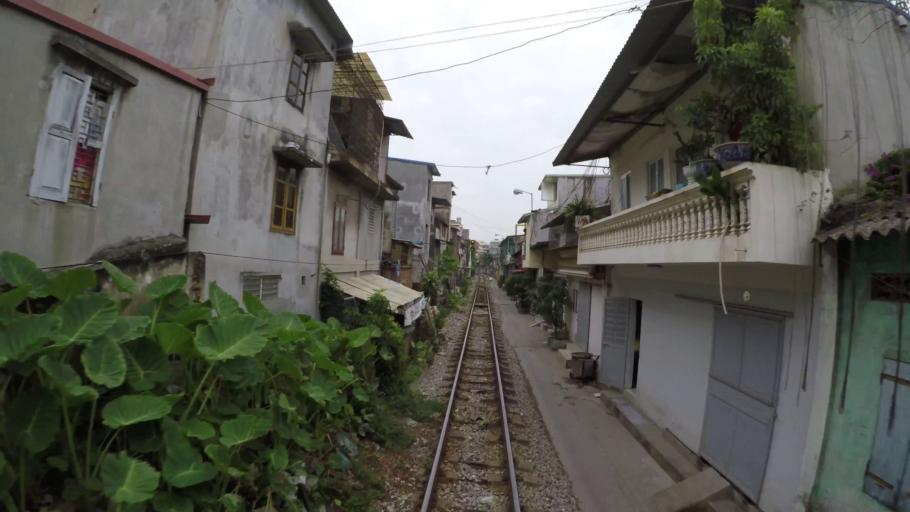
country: VN
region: Hai Phong
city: Haiphong
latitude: 20.8539
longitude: 106.6665
